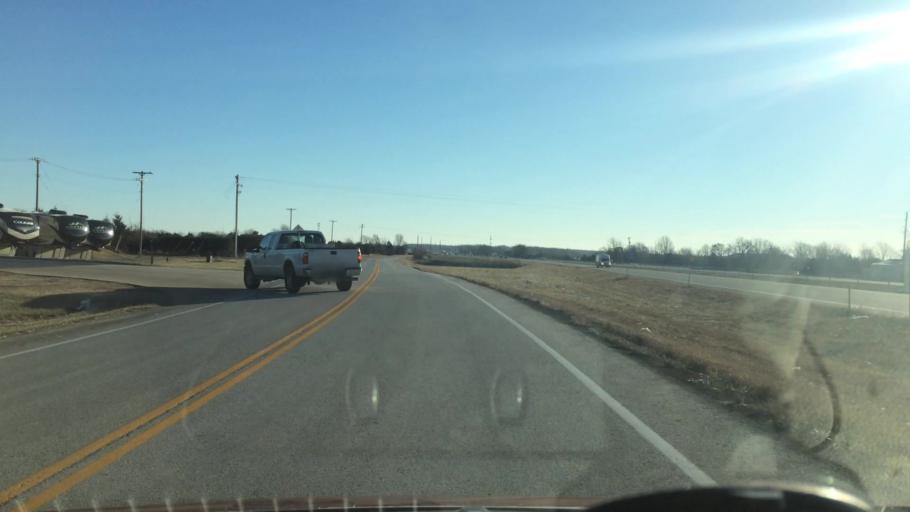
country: US
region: Missouri
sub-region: Greene County
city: Strafford
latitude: 37.2718
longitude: -93.1058
